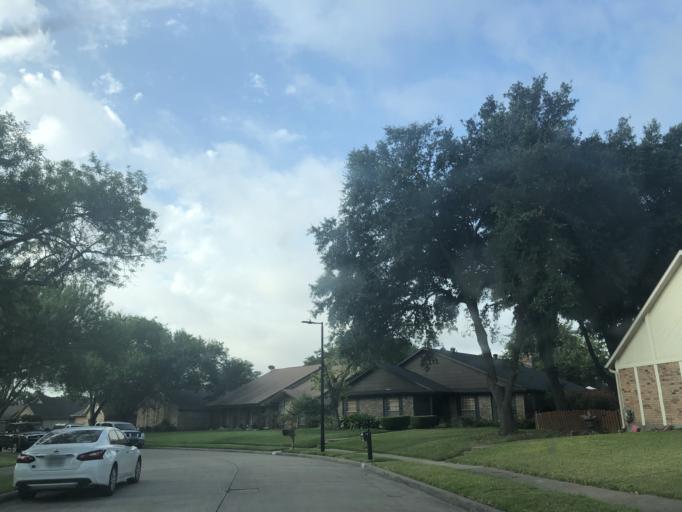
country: US
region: Texas
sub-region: Dallas County
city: Garland
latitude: 32.8527
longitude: -96.6314
